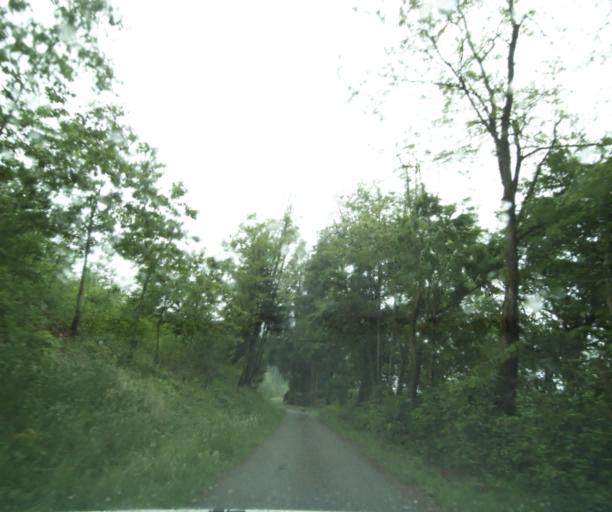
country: FR
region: Bourgogne
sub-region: Departement de Saone-et-Loire
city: Charolles
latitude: 46.3777
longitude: 4.3595
